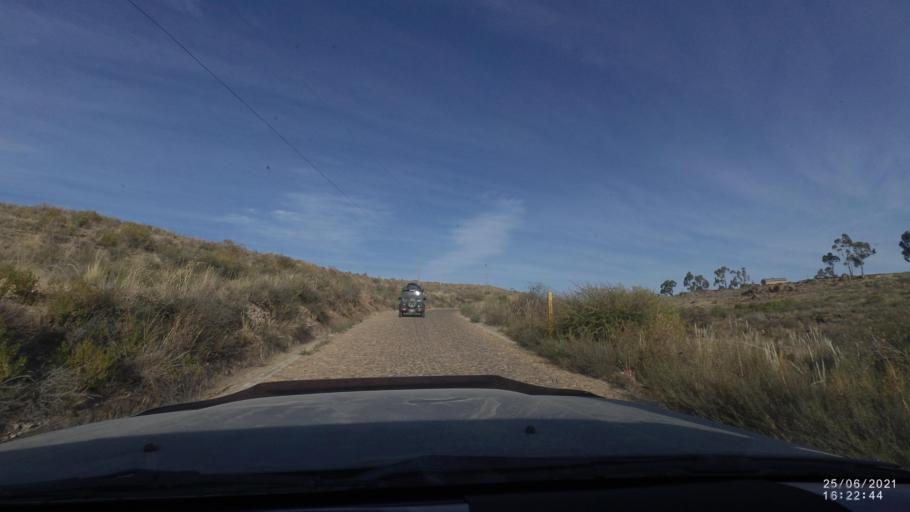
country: BO
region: Cochabamba
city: Cliza
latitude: -17.7565
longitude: -65.8336
